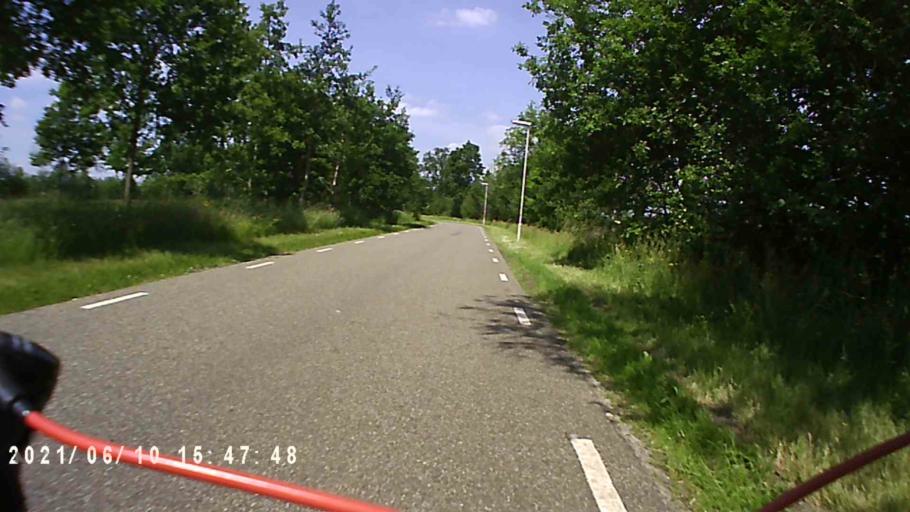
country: NL
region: Friesland
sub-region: Gemeente Smallingerland
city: Rottevalle
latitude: 53.1623
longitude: 6.1182
